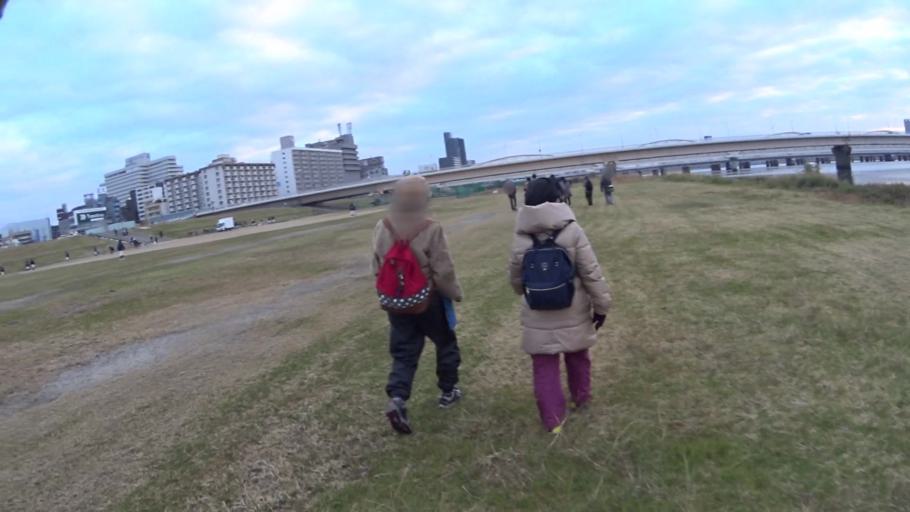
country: JP
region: Osaka
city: Osaka-shi
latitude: 34.7132
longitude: 135.4799
